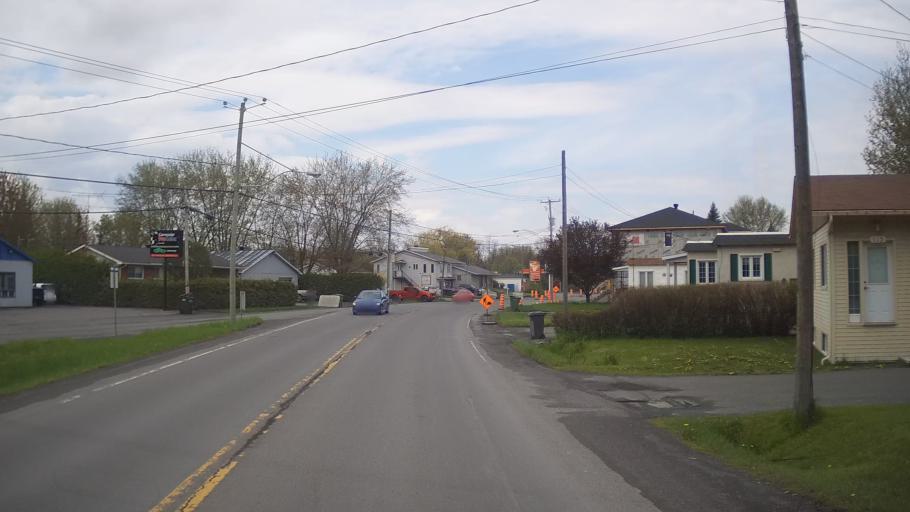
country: CA
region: Quebec
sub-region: Monteregie
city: Saint-Jean-sur-Richelieu
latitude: 45.3132
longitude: -73.2098
